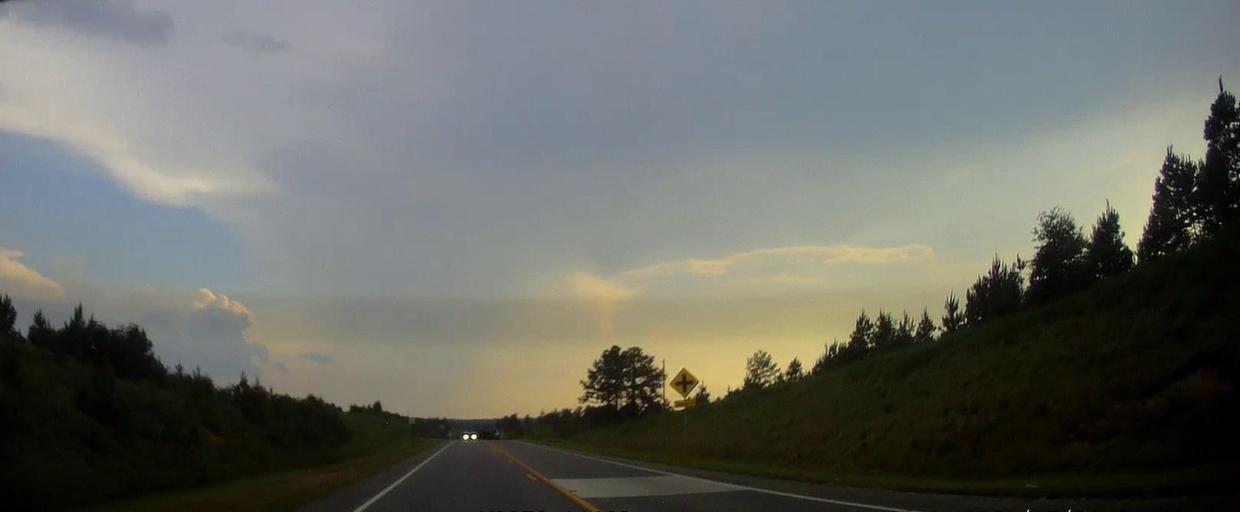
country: US
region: Georgia
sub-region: Laurens County
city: East Dublin
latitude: 32.6235
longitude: -82.8770
